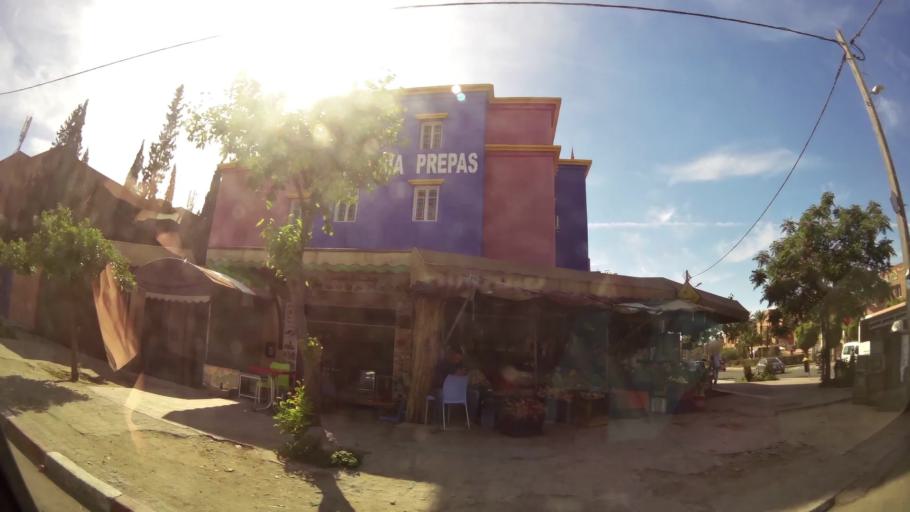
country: MA
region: Marrakech-Tensift-Al Haouz
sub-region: Marrakech
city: Marrakesh
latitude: 31.6550
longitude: -8.0108
